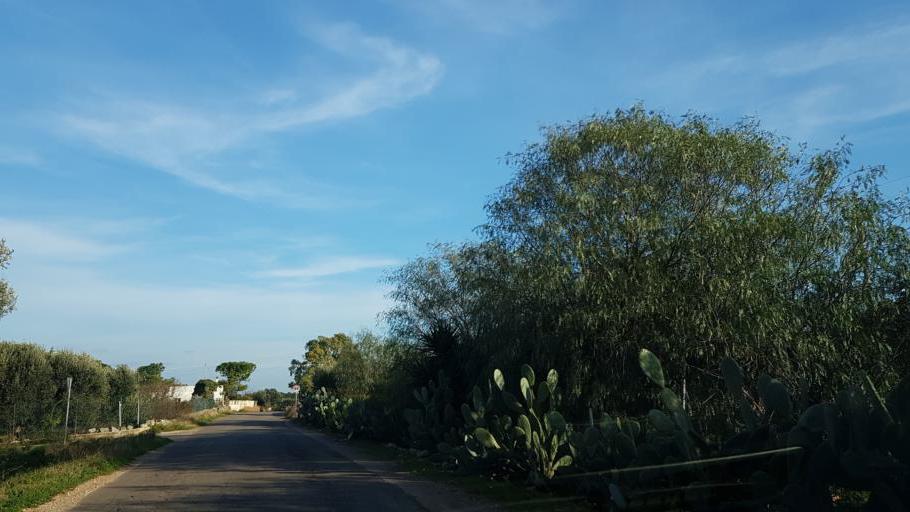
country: IT
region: Apulia
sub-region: Provincia di Brindisi
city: San Vito dei Normanni
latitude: 40.6963
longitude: 17.7463
